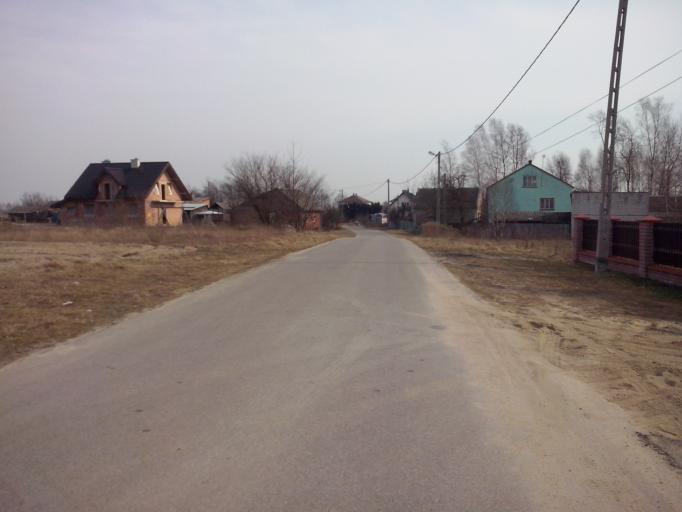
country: PL
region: Subcarpathian Voivodeship
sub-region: Powiat nizanski
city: Krzeszow
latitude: 50.4237
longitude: 22.3622
